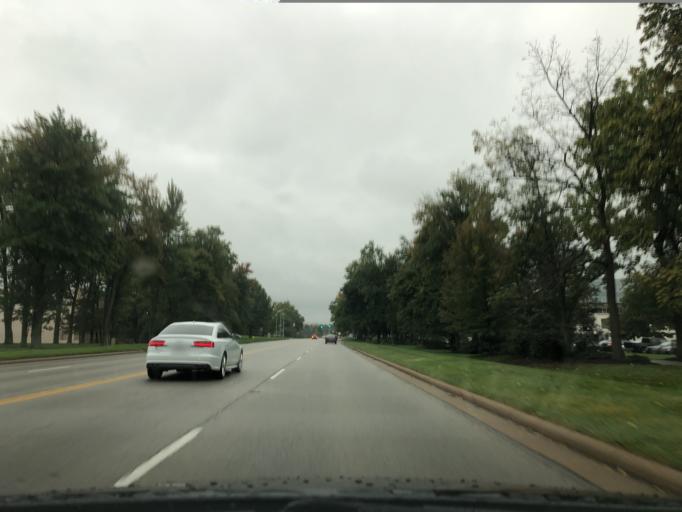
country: US
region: Ohio
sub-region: Hamilton County
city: Blue Ash
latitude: 39.2569
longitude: -84.3805
